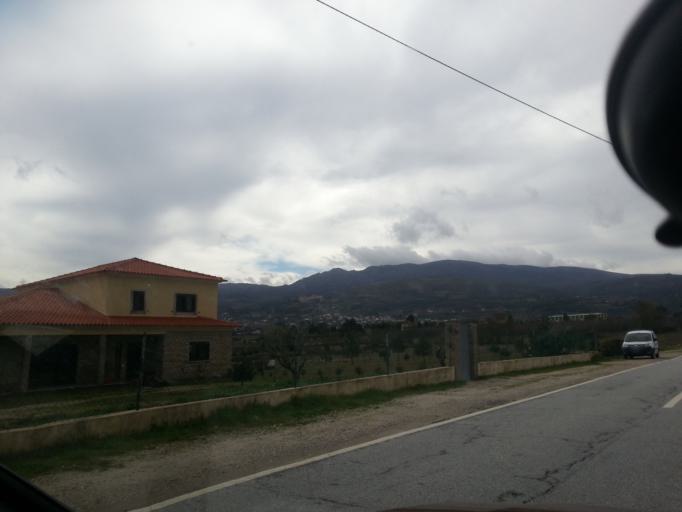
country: PT
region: Guarda
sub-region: Fornos de Algodres
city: Fornos de Algodres
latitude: 40.5433
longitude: -7.5693
